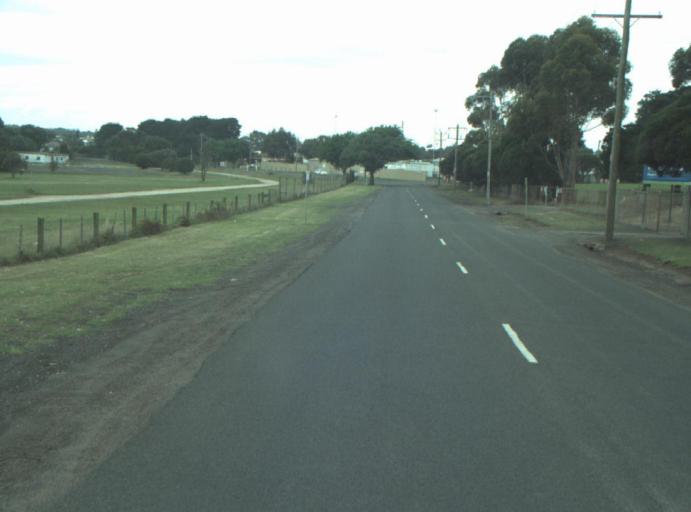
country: AU
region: Victoria
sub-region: Greater Geelong
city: Breakwater
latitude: -38.1745
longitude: 144.3708
